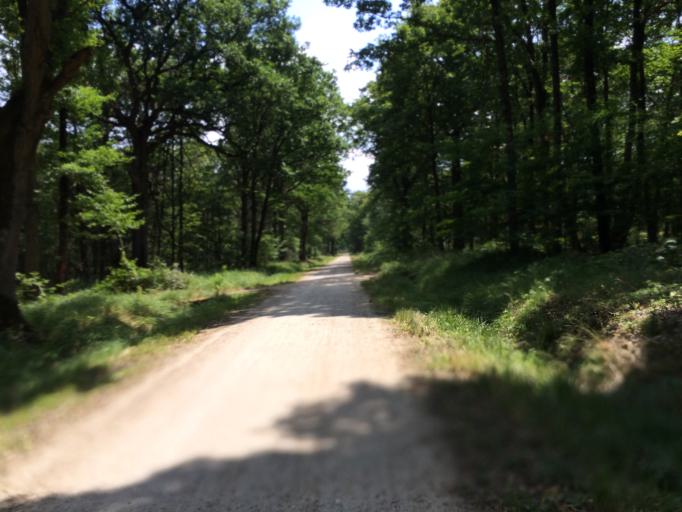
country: FR
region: Ile-de-France
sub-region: Departement de l'Essonne
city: Brunoy
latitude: 48.6726
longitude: 2.4949
